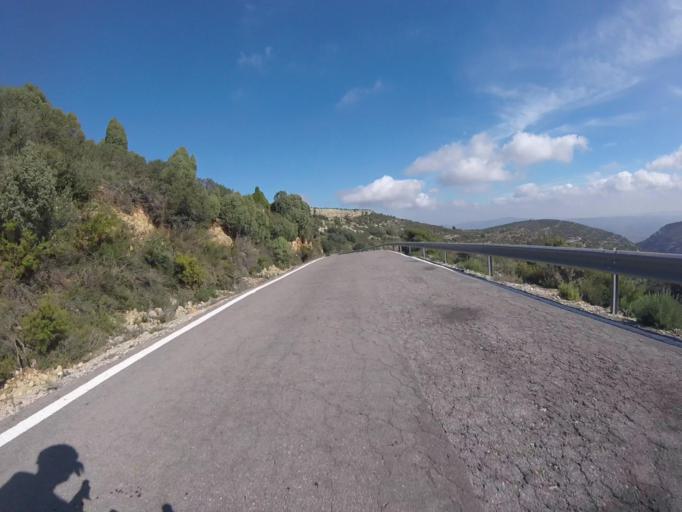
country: ES
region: Valencia
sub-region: Provincia de Castello
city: Albocasser
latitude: 40.3361
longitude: 0.0427
